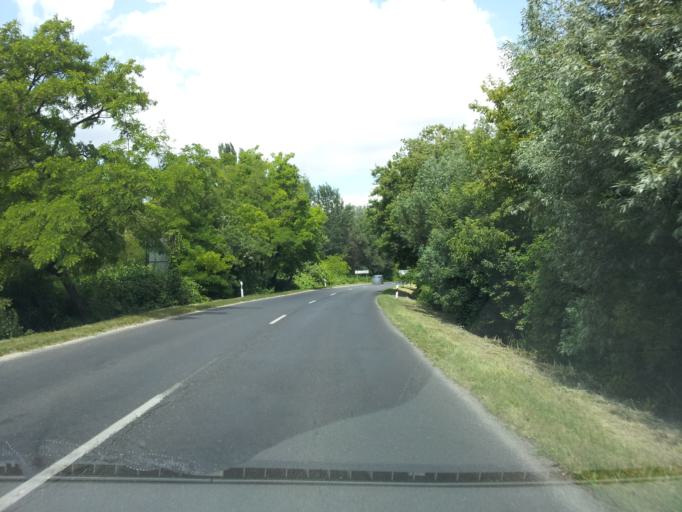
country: HU
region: Veszprem
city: Balatonalmadi
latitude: 47.0451
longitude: 18.0595
